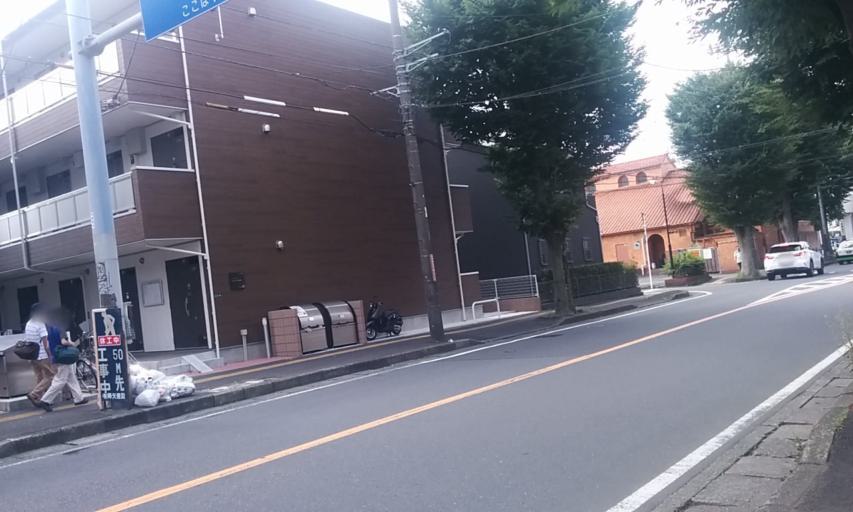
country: JP
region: Tokyo
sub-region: Machida-shi
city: Machida
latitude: 35.5625
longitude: 139.3983
